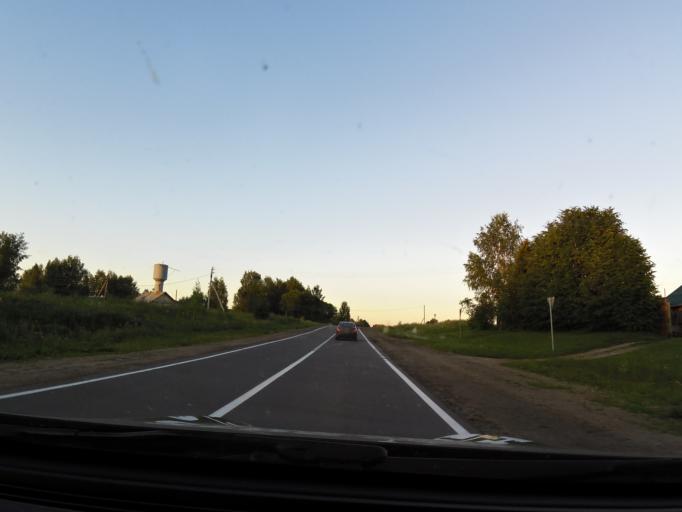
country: RU
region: Jaroslavl
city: Lyubim
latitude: 58.3588
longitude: 40.5448
